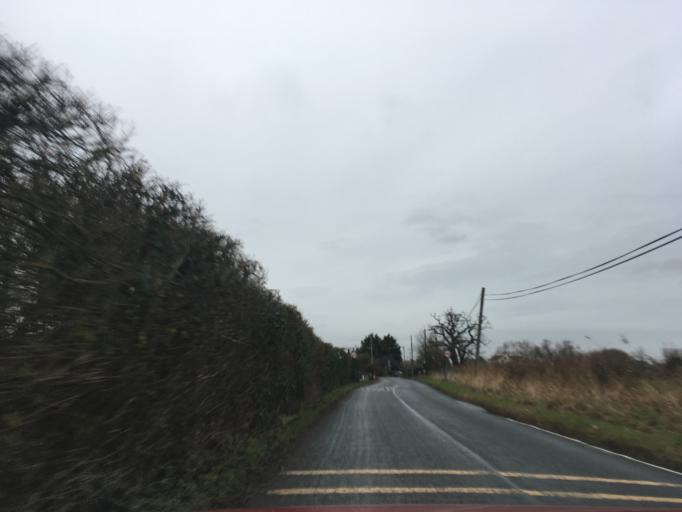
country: GB
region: Wales
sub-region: Newport
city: Nash
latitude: 51.5499
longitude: -2.9403
